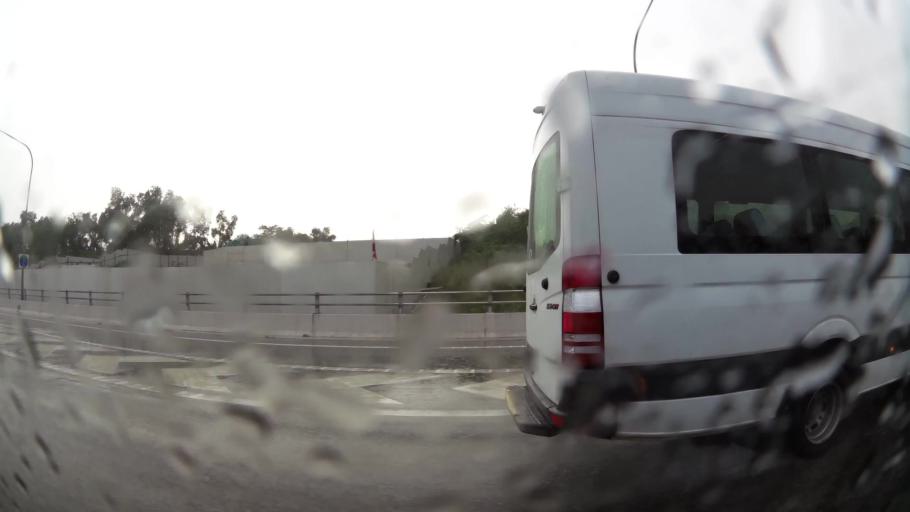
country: MY
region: Johor
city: Kampung Pasir Gudang Baru
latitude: 1.3840
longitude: 103.9158
